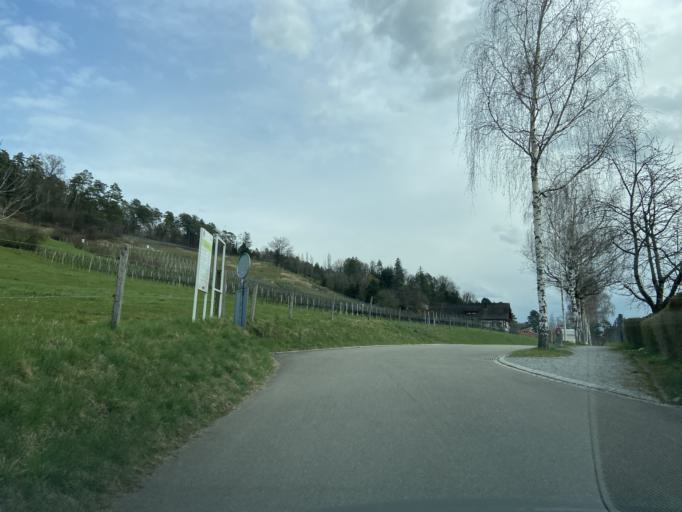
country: CH
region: Zurich
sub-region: Bezirk Winterthur
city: Wuelflingen (Kreis 6) / Lindenplatz
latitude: 47.5149
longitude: 8.6991
